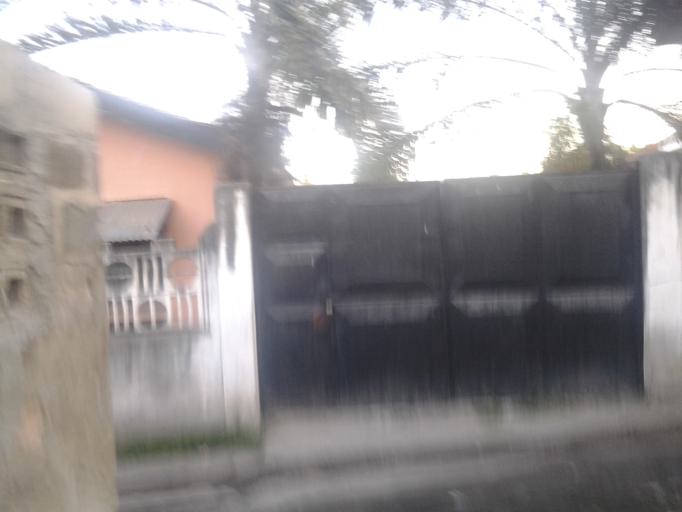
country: TZ
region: Dar es Salaam
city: Magomeni
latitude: -6.8357
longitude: 39.2218
